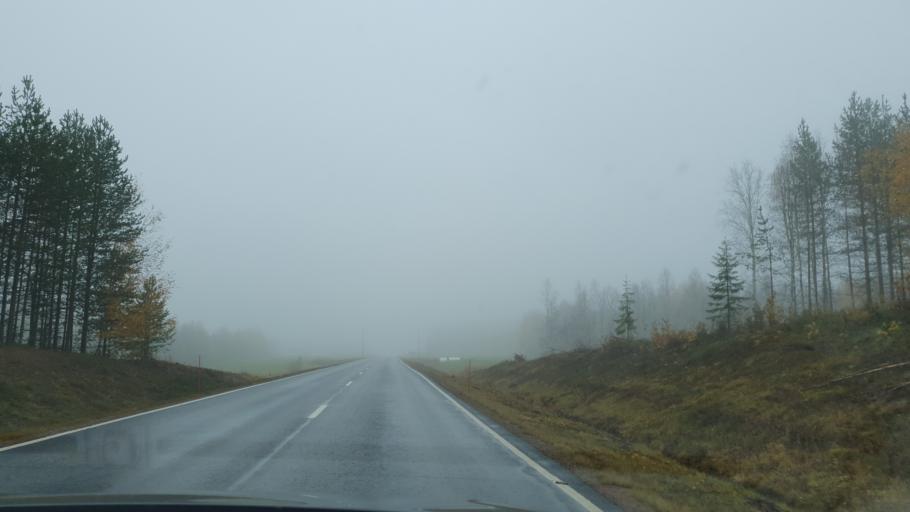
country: FI
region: Lapland
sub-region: Rovaniemi
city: Rovaniemi
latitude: 66.8035
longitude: 25.4132
